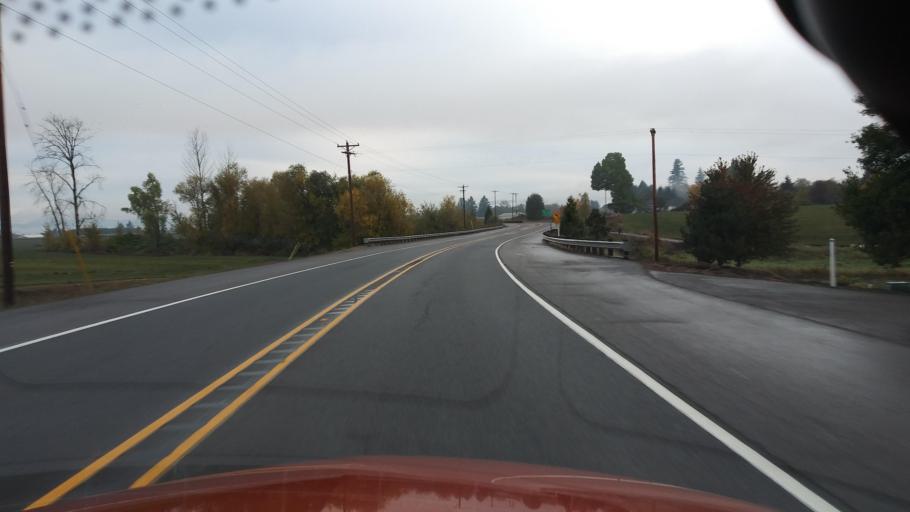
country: US
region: Oregon
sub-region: Washington County
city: Cornelius
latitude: 45.5484
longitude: -123.0613
